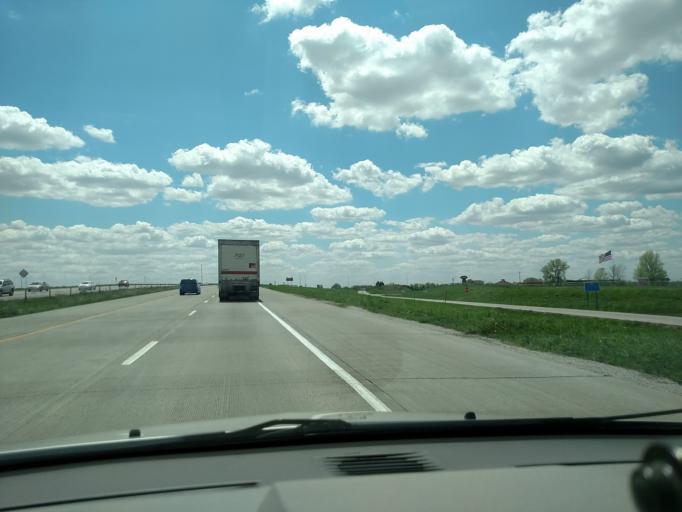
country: US
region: Iowa
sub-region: Polk County
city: Ankeny
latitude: 41.7646
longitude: -93.5697
